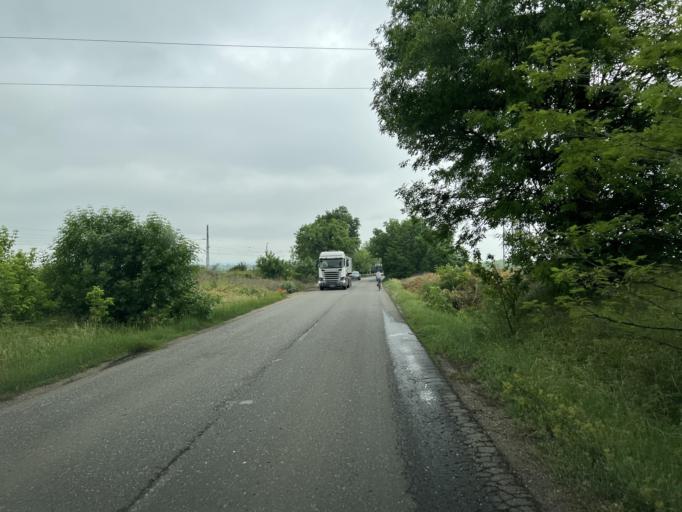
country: HU
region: Pest
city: Tura
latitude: 47.6351
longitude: 19.6341
